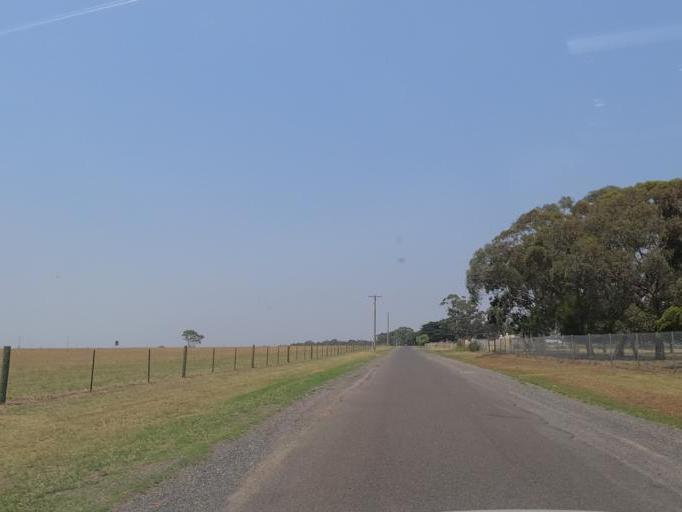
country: AU
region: Victoria
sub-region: Hume
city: Greenvale
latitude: -37.6394
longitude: 144.8295
